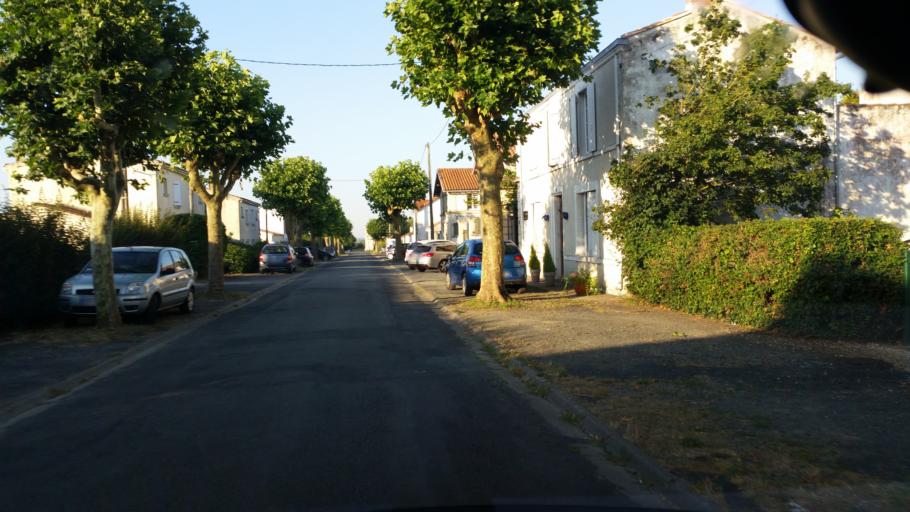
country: FR
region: Poitou-Charentes
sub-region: Departement de la Charente-Maritime
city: Marans
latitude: 46.3065
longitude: -1.0000
